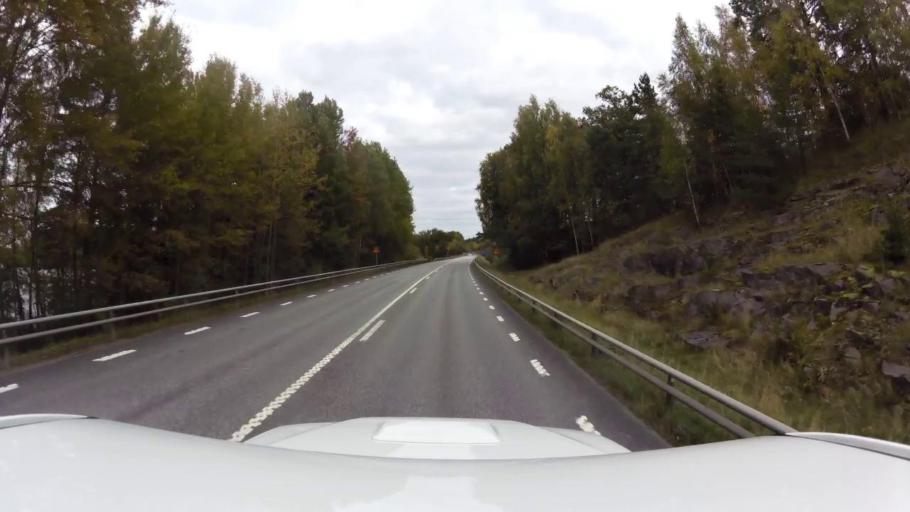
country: SE
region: OEstergoetland
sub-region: Kinda Kommun
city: Rimforsa
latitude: 58.1670
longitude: 15.6778
